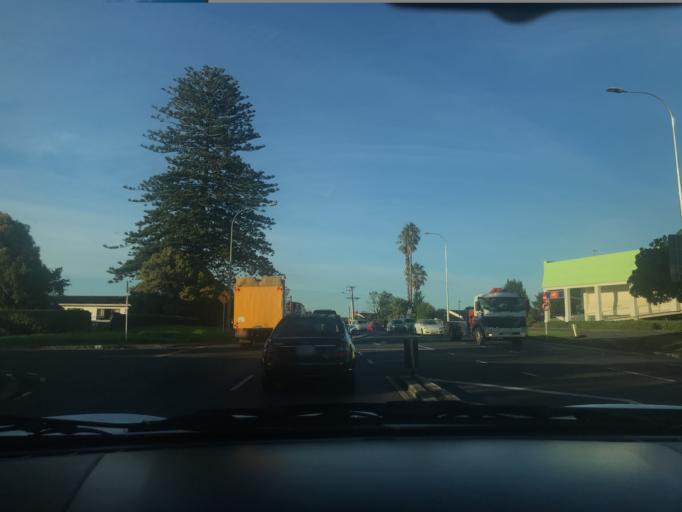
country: NZ
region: Auckland
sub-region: Auckland
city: Tamaki
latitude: -36.9094
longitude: 174.8383
